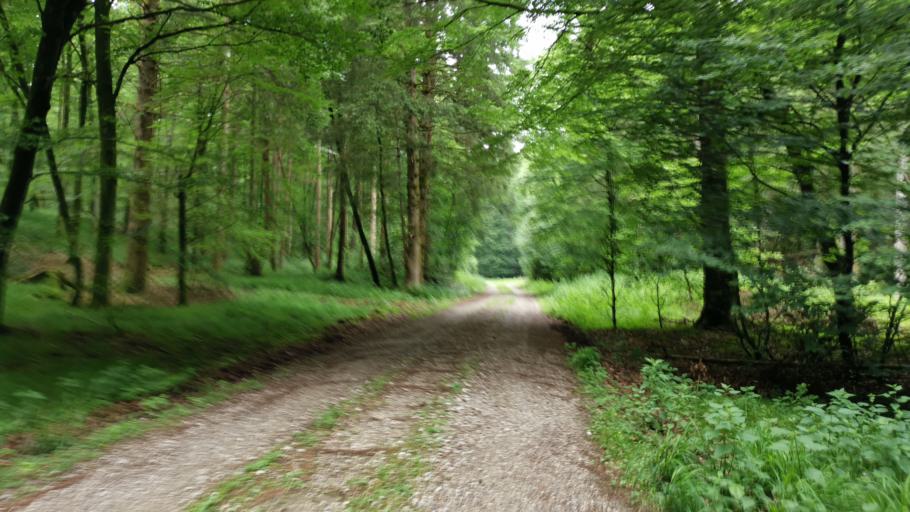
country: DE
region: Bavaria
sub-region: Upper Bavaria
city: Schaftlarn
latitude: 48.0248
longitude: 11.4387
